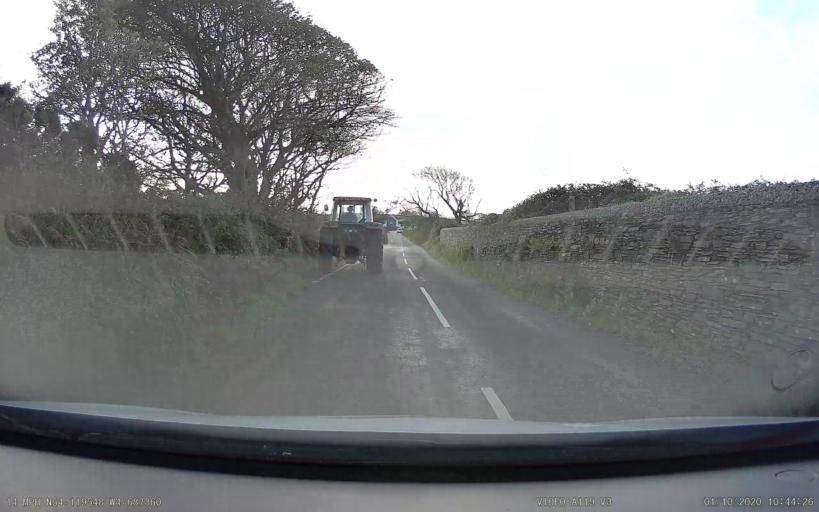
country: IM
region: Castletown
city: Castletown
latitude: 54.1196
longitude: -4.6873
